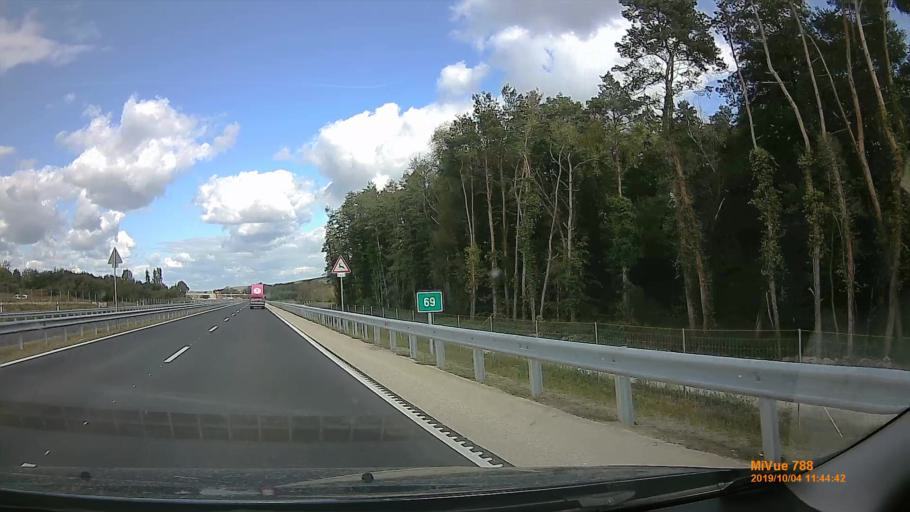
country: HU
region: Somogy
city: Karad
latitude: 46.6168
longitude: 17.7973
